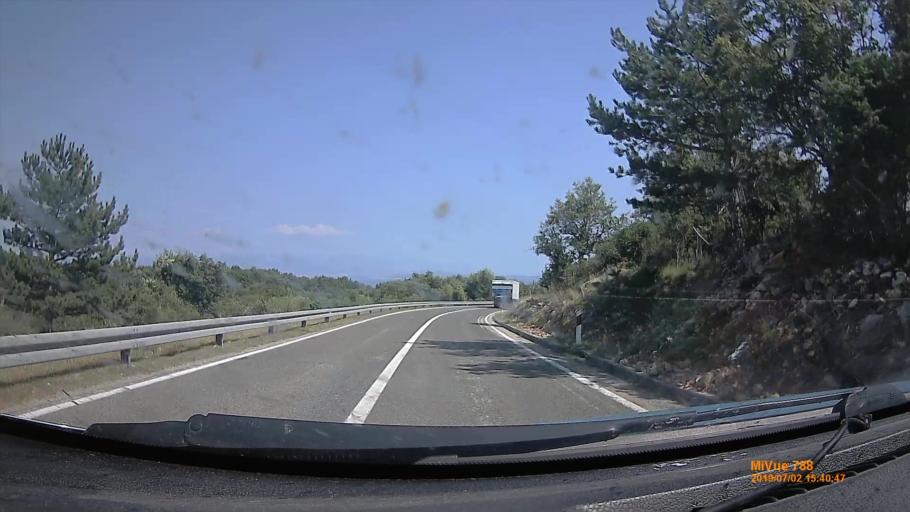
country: HR
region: Primorsko-Goranska
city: Cres
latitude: 44.9634
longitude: 14.4348
